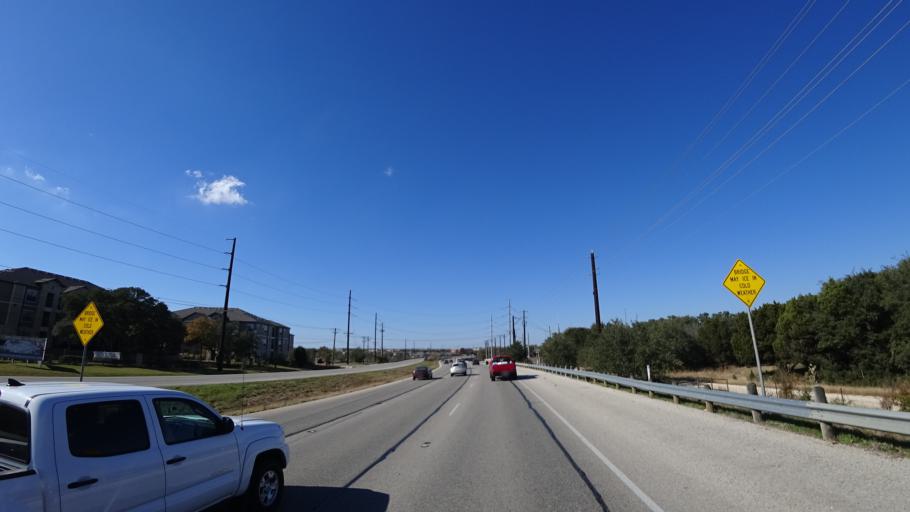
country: US
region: Texas
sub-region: Williamson County
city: Jollyville
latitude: 30.4632
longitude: -97.7562
